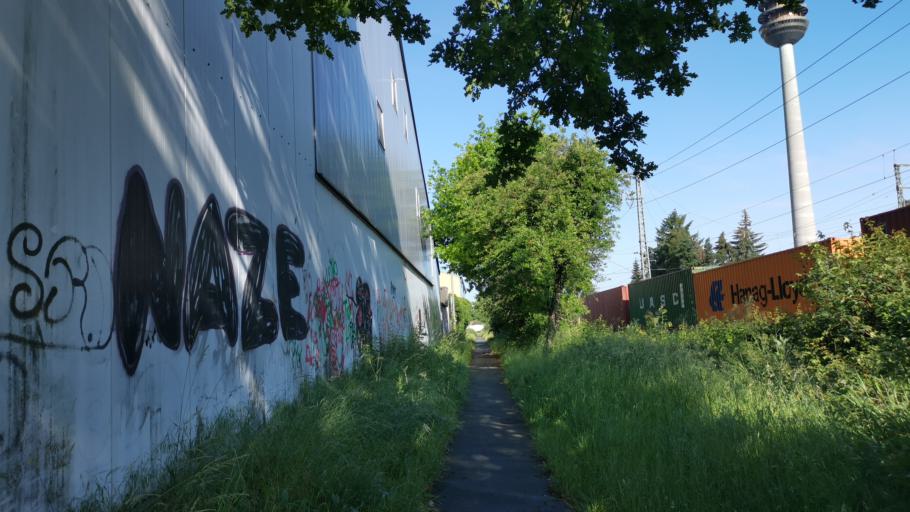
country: DE
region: Bavaria
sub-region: Regierungsbezirk Mittelfranken
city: Grossreuth bei Schweinau
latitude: 49.4232
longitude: 11.0446
